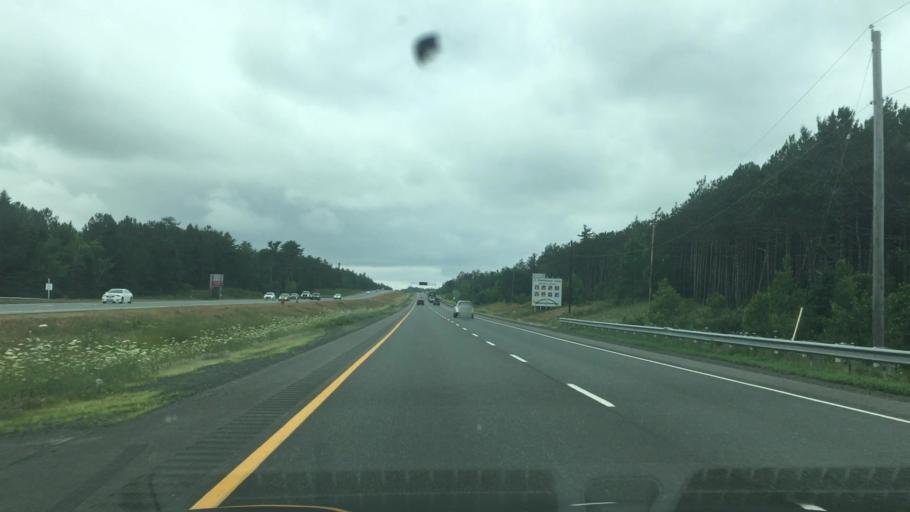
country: CA
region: Nova Scotia
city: Truro
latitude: 45.3988
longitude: -63.4418
